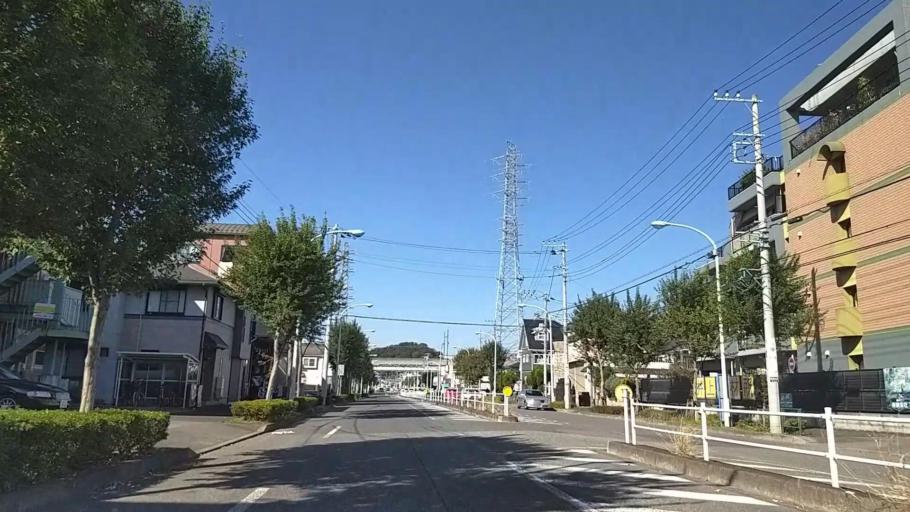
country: JP
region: Tokyo
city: Hachioji
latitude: 35.5977
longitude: 139.3667
